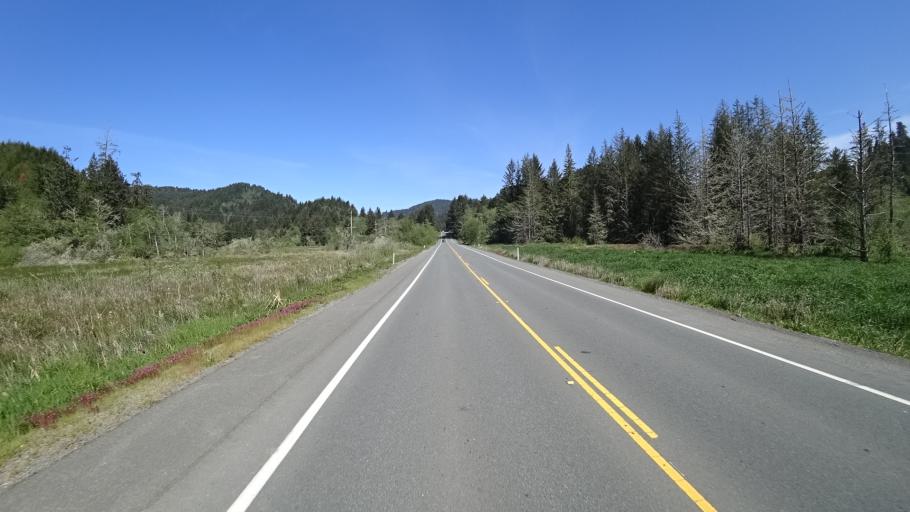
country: US
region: California
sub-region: Del Norte County
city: Bertsch-Oceanview
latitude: 41.5690
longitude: -124.0695
